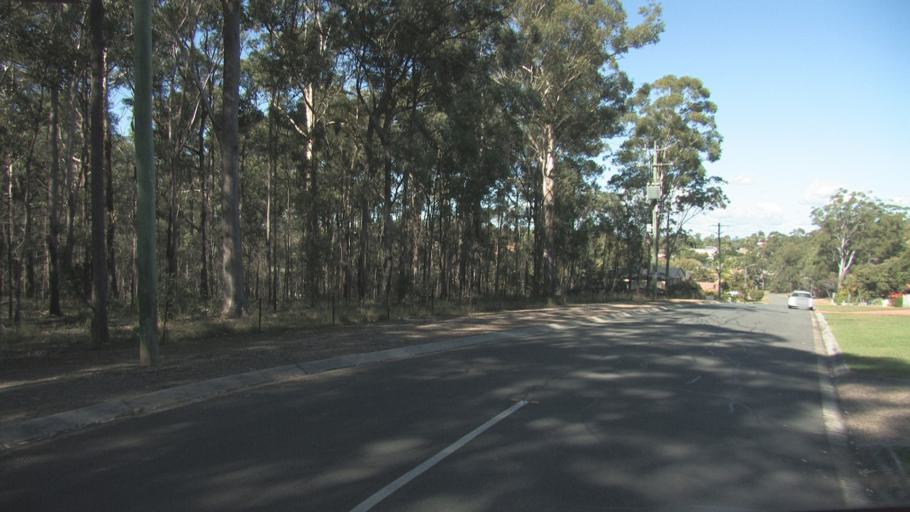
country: AU
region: Queensland
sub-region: Logan
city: Slacks Creek
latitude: -27.6399
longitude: 153.1874
